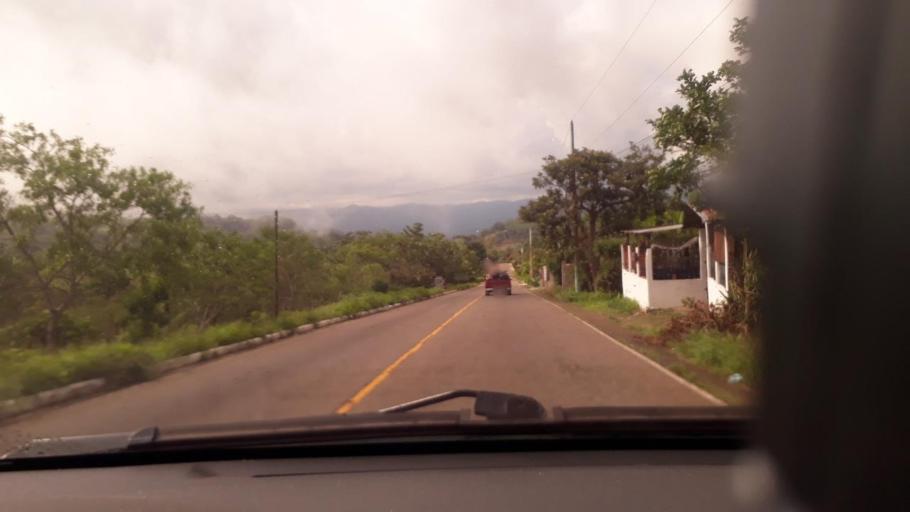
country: GT
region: Jutiapa
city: Quesada
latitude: 14.2059
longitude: -90.0246
